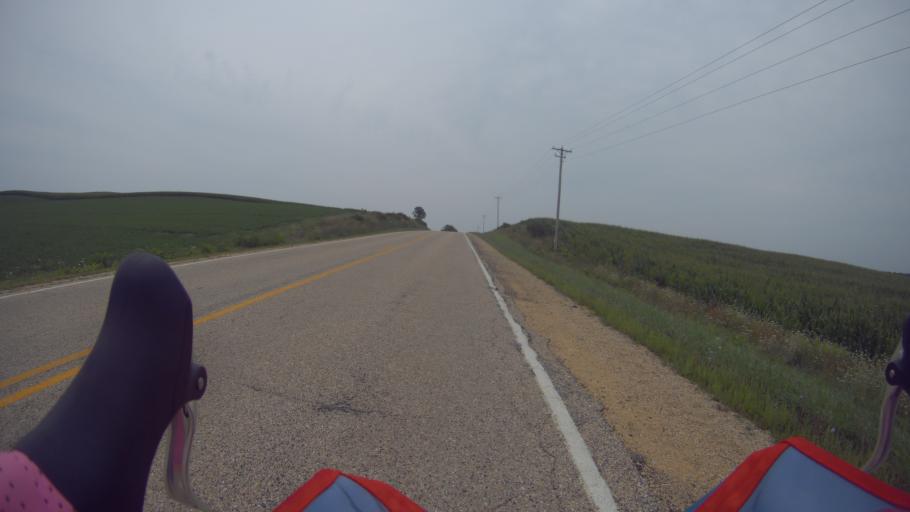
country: US
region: Wisconsin
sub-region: Dane County
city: Belleville
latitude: 42.9082
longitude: -89.5860
